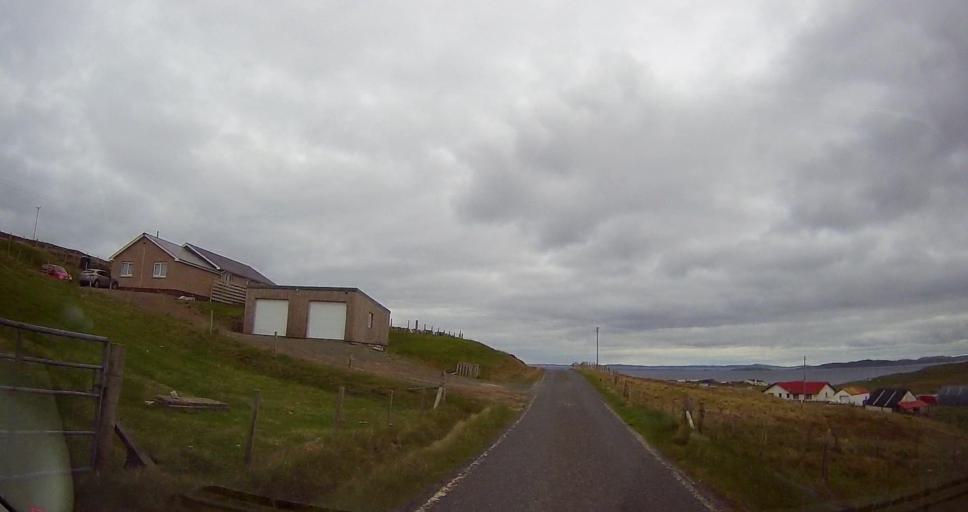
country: GB
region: Scotland
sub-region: Shetland Islands
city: Shetland
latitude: 60.5039
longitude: -1.0595
